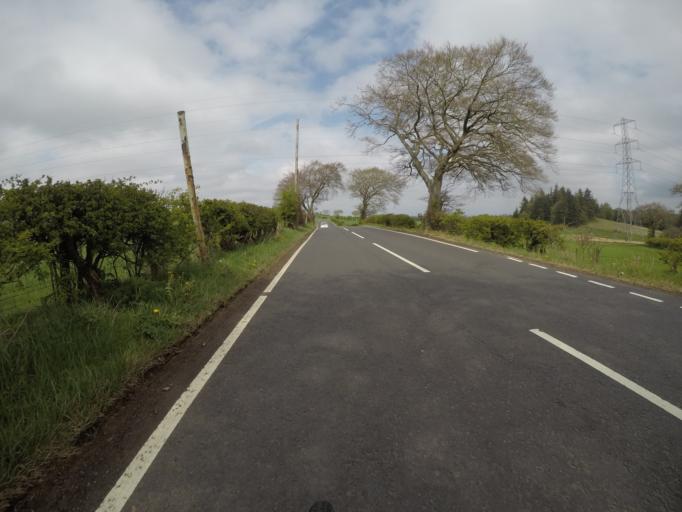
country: GB
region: Scotland
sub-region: East Renfrewshire
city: Barrhead
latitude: 55.7658
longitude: -4.3748
